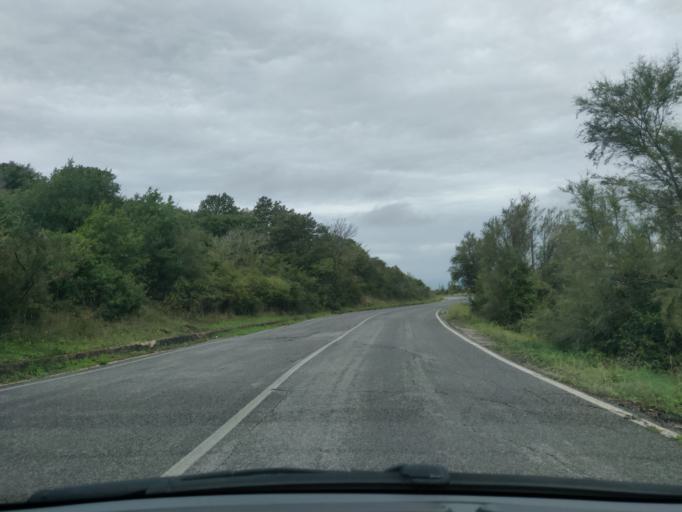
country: IT
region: Latium
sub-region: Citta metropolitana di Roma Capitale
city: Civitavecchia
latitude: 42.1116
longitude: 11.8514
